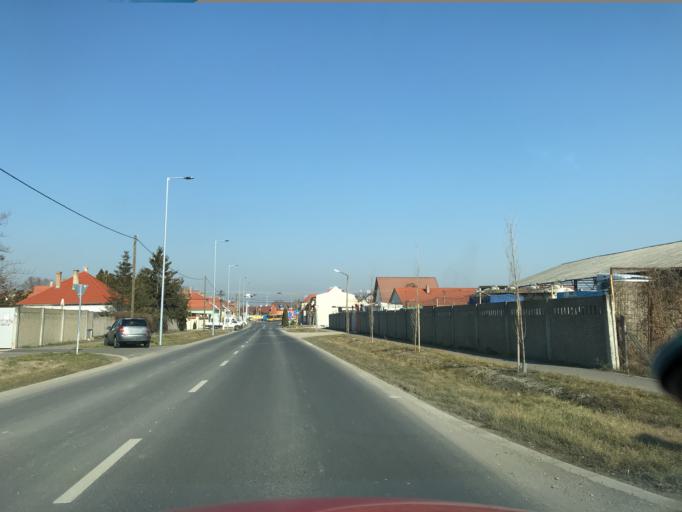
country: HU
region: Gyor-Moson-Sopron
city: Gyor
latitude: 47.6801
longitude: 17.6106
